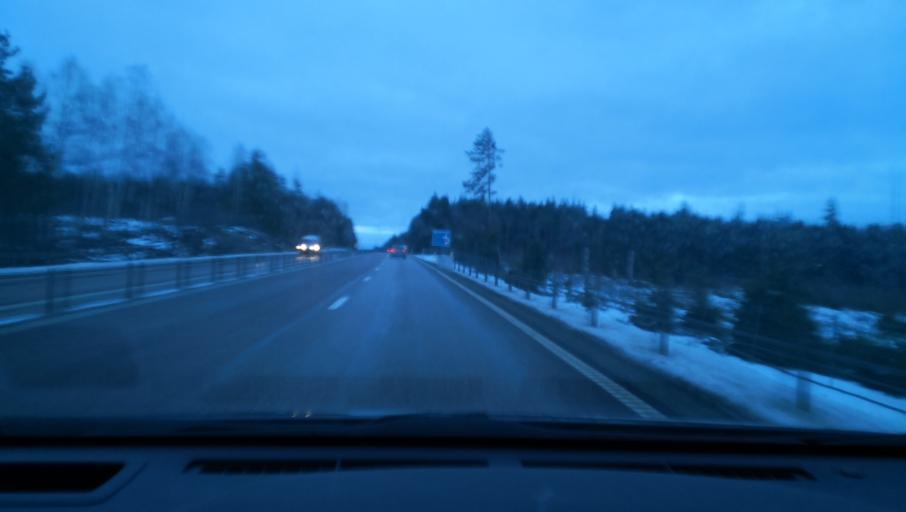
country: SE
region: Vaestmanland
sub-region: Surahammars Kommun
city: Ramnas
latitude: 59.8347
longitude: 16.0734
